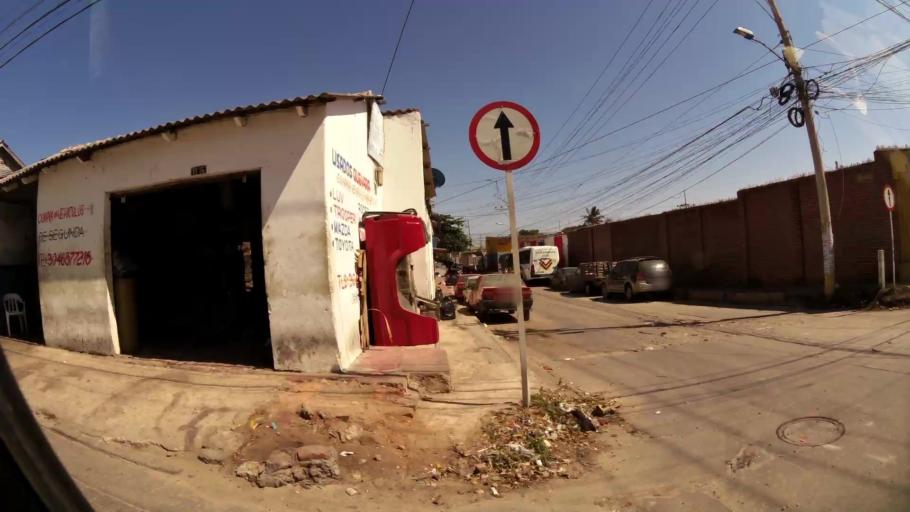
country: CO
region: Atlantico
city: Barranquilla
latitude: 10.9693
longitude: -74.7854
